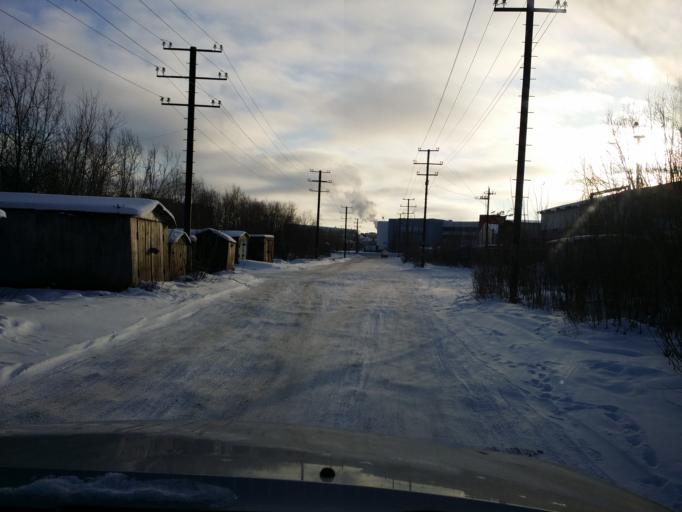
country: RU
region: Khanty-Mansiyskiy Avtonomnyy Okrug
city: Megion
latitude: 61.0431
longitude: 76.1029
